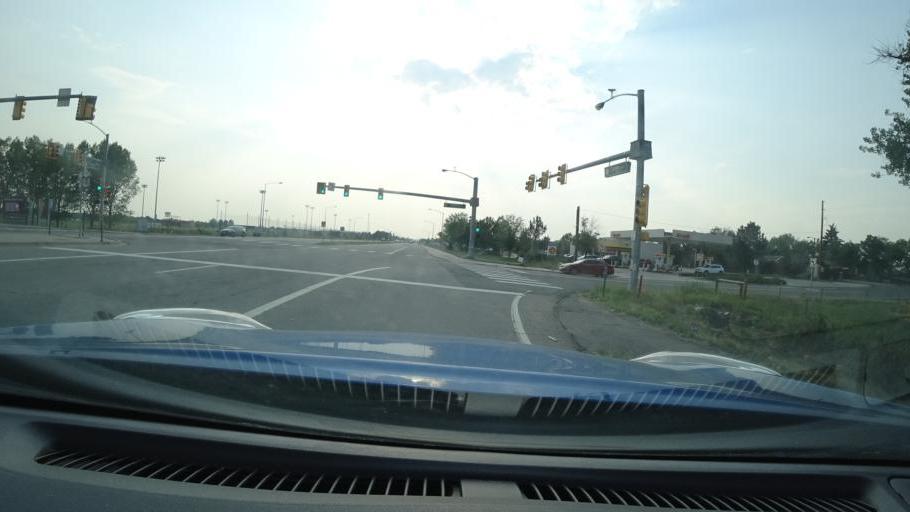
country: US
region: Colorado
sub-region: Adams County
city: Aurora
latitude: 39.7403
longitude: -104.7627
